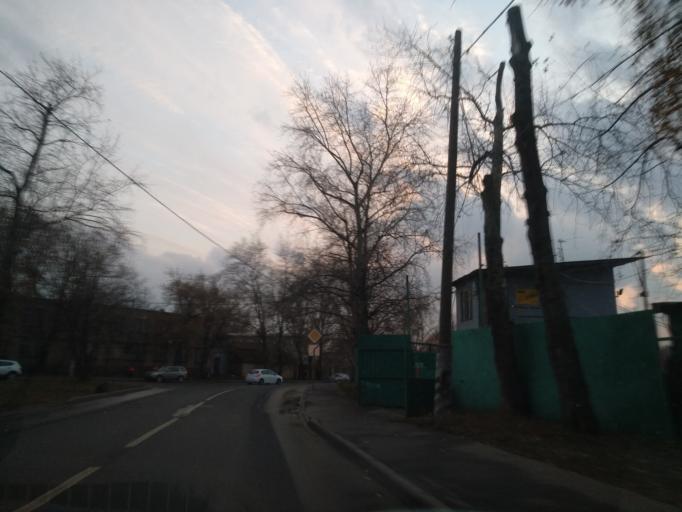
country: RU
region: Moscow
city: Leonovo
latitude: 55.8646
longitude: 37.6496
